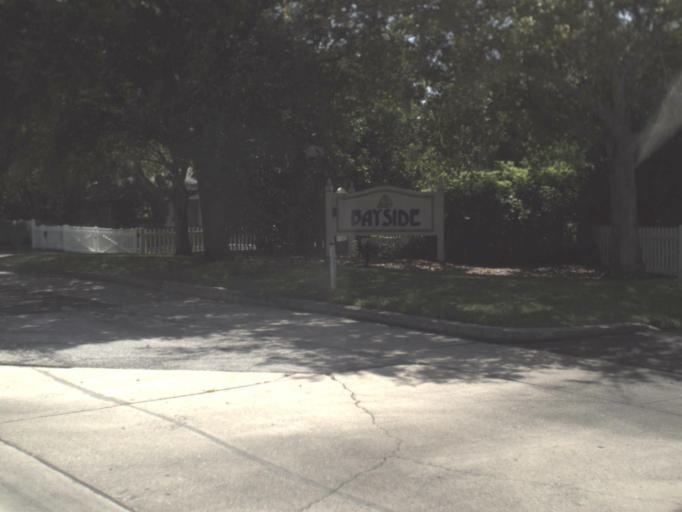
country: US
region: Florida
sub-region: Pinellas County
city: Clearwater
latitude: 27.9879
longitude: -82.7959
